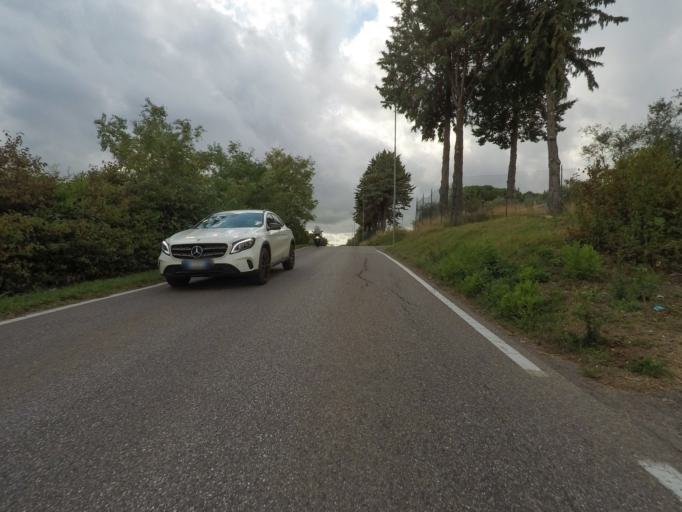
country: IT
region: Tuscany
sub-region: Provincia di Siena
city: Belverde
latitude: 43.3464
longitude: 11.3135
